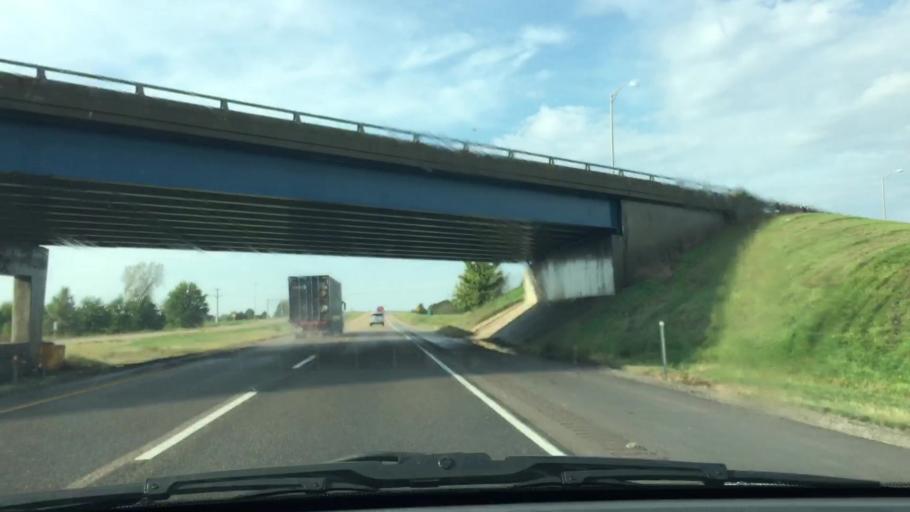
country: US
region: Illinois
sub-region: Whiteside County
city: Rock Falls
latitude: 41.7583
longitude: -89.6371
